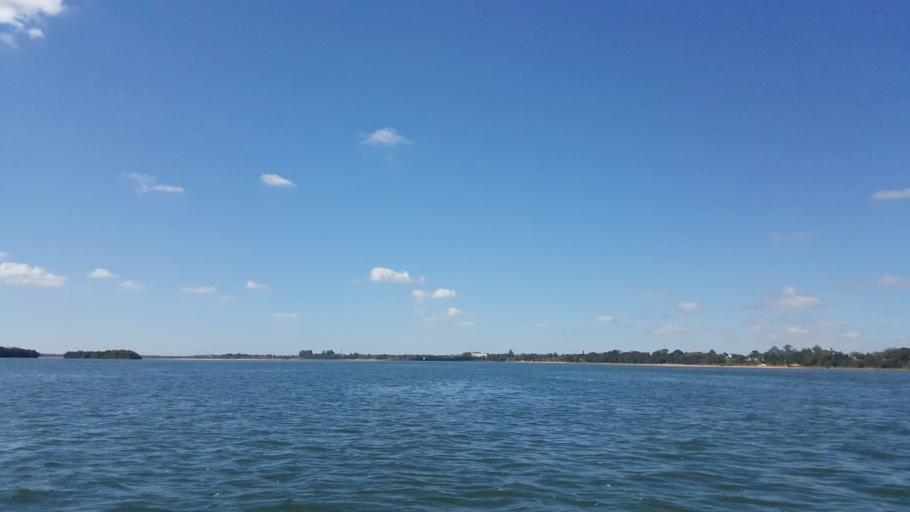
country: AR
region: Corrientes
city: Ituzaingo
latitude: -27.5819
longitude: -56.7023
